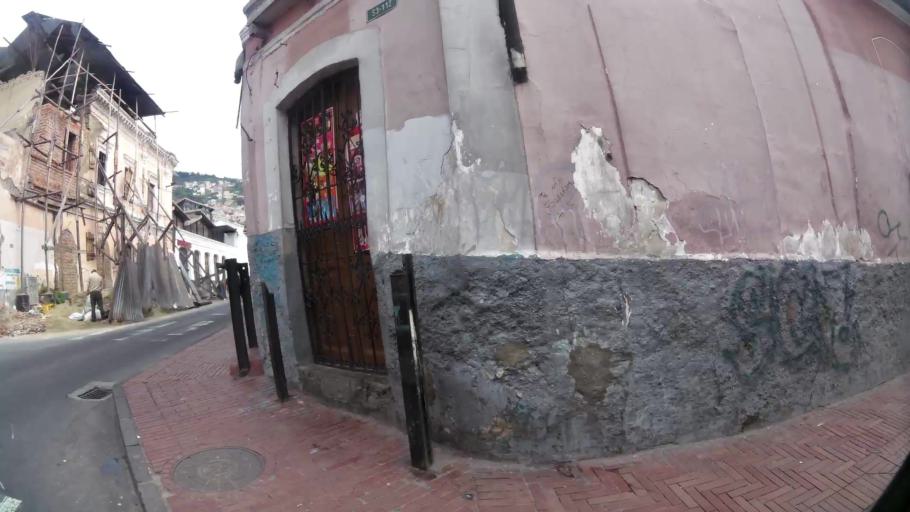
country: EC
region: Pichincha
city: Quito
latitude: -0.2239
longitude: -78.5174
